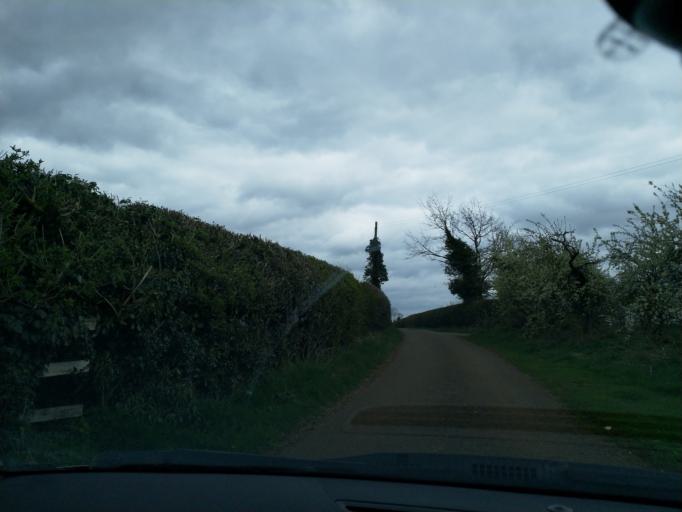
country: GB
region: England
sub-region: Oxfordshire
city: Hanwell
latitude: 52.1157
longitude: -1.4689
